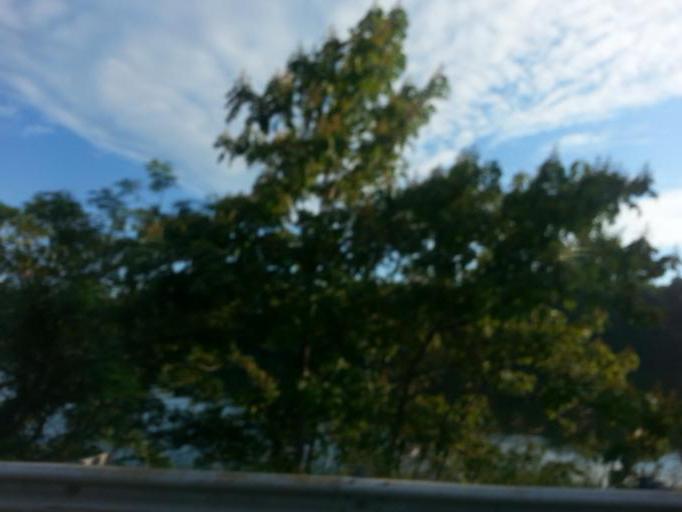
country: US
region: Alabama
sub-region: Lauderdale County
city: Rogersville
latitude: 34.8443
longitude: -87.3746
